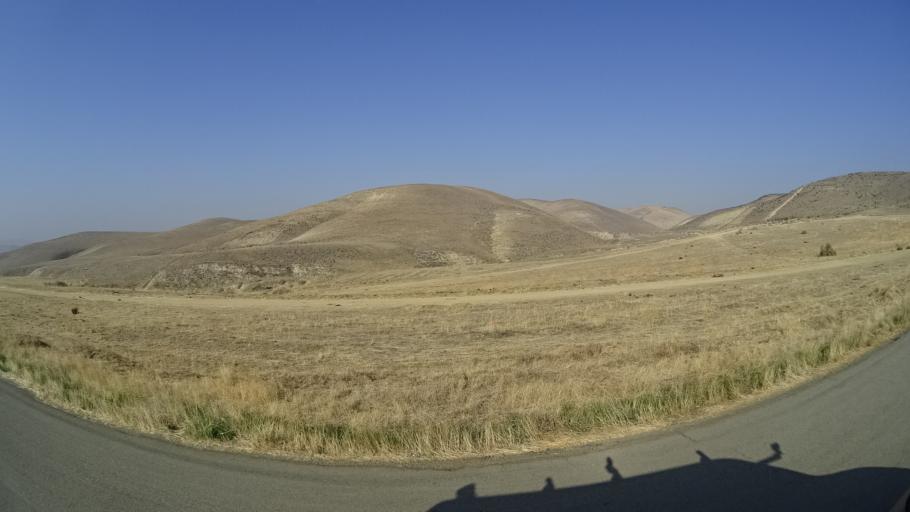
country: US
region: California
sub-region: Kern County
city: Oildale
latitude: 35.4382
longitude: -118.8257
